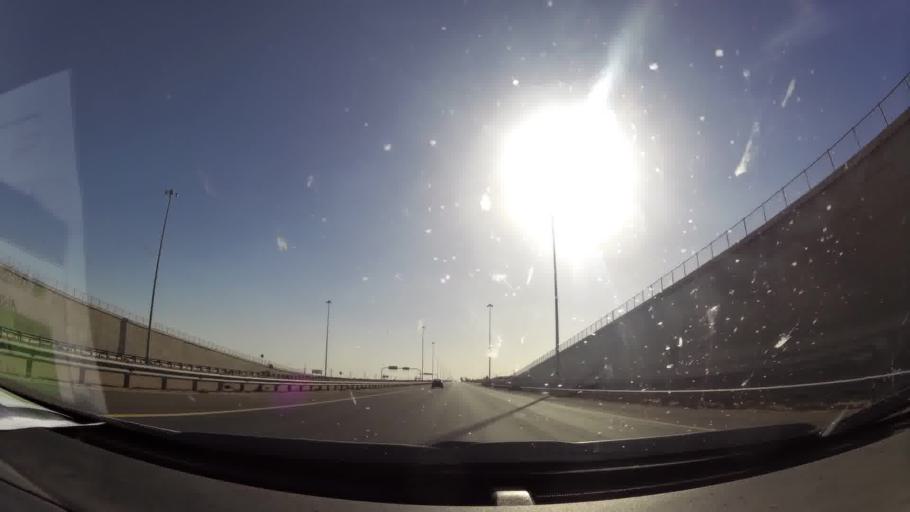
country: KW
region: Muhafazat al Jahra'
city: Al Jahra'
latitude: 29.4737
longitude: 47.7677
